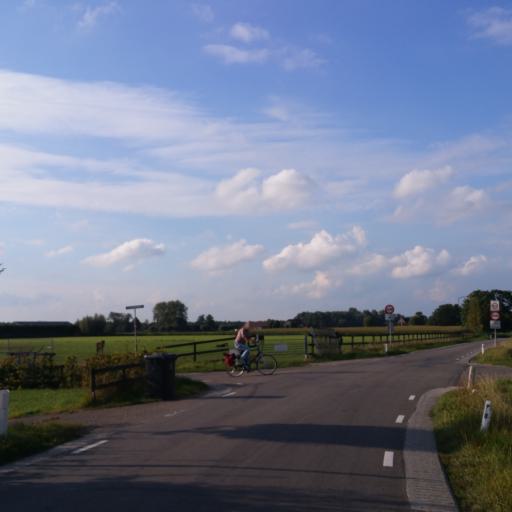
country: NL
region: Utrecht
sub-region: Gemeente IJsselstein
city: IJsselstein
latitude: 52.0436
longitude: 5.0105
